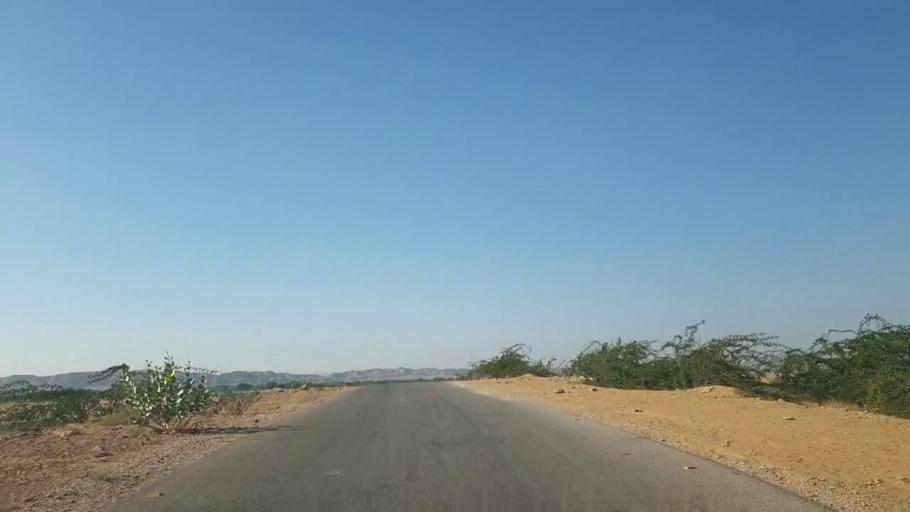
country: PK
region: Sindh
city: Malir Cantonment
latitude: 25.2819
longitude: 67.5823
